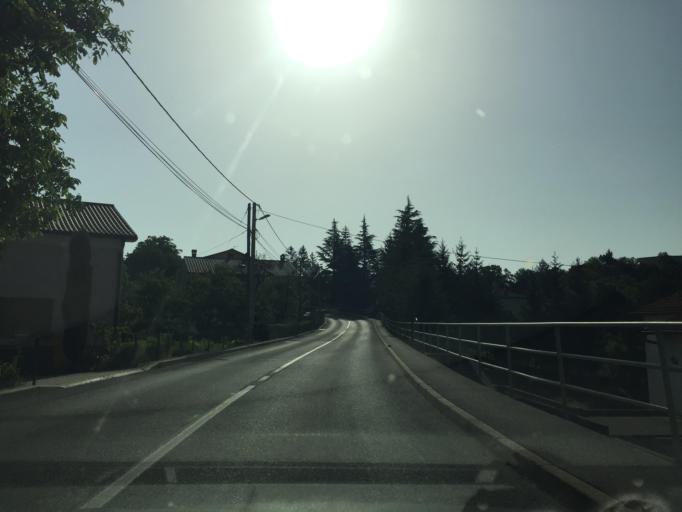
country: HR
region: Primorsko-Goranska
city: Klana
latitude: 45.4425
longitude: 14.3689
